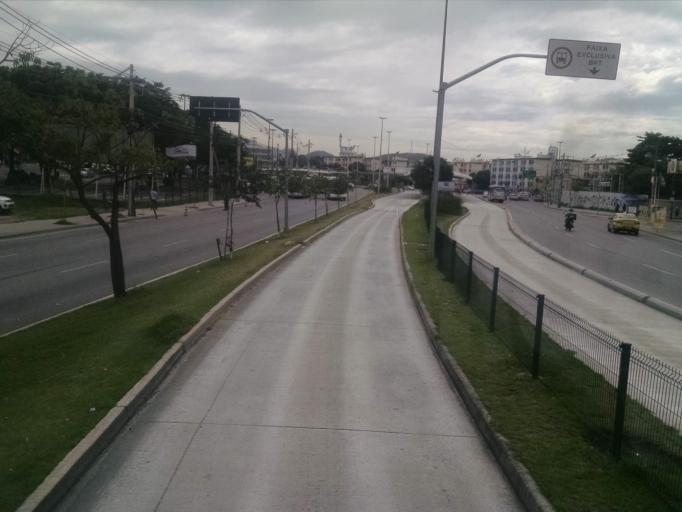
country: BR
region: Rio de Janeiro
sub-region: Sao Joao De Meriti
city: Sao Joao de Meriti
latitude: -22.9369
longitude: -43.3720
